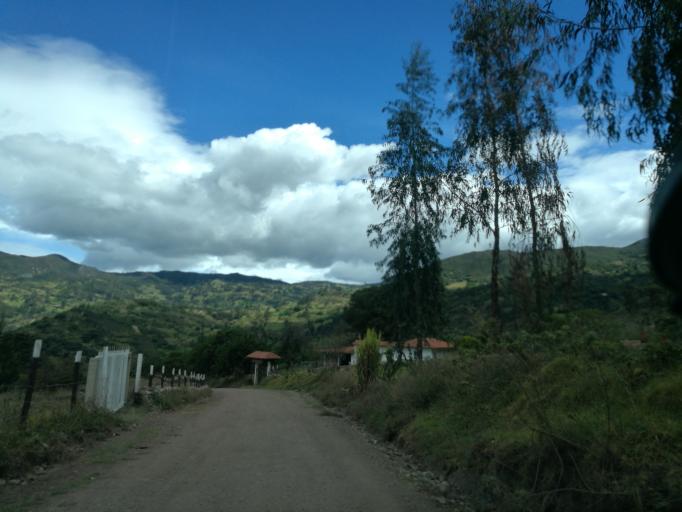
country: CO
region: Boyaca
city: Socota
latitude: 6.1196
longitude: -72.7144
